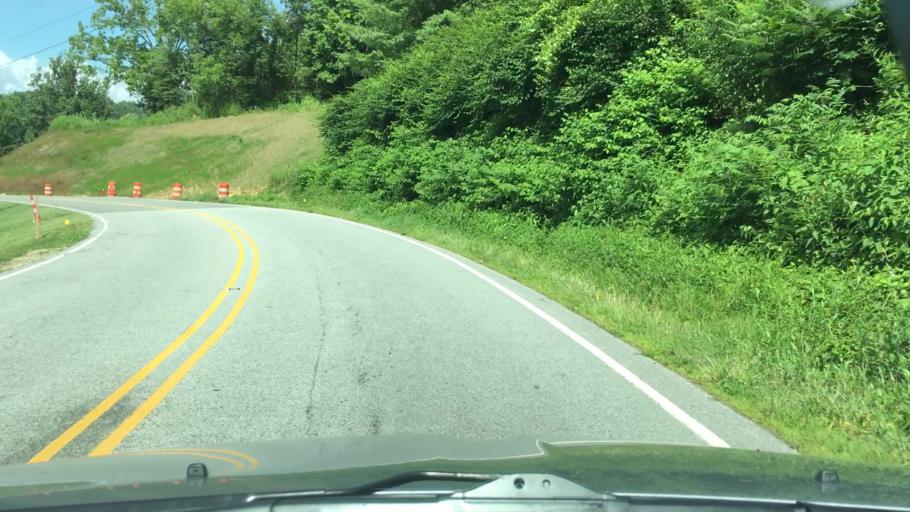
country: US
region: North Carolina
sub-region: Yancey County
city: Burnsville
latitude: 35.9081
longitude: -82.2136
